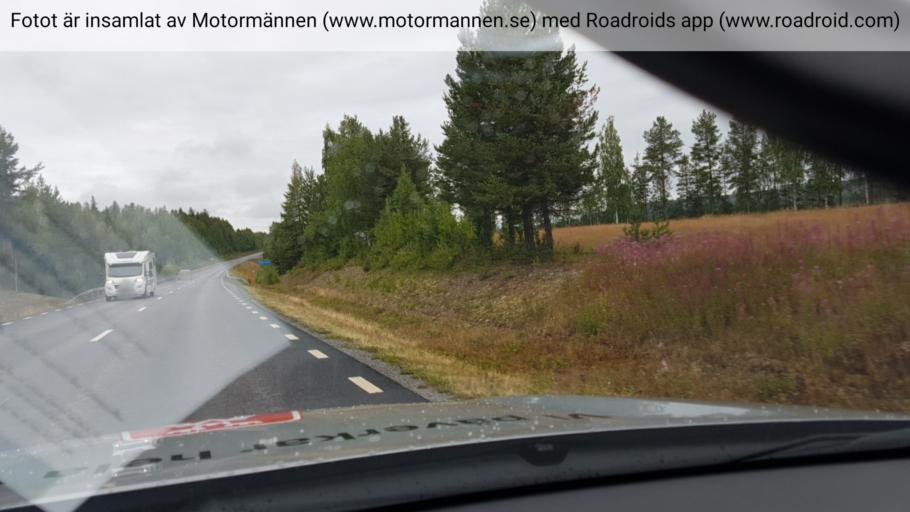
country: SE
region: Norrbotten
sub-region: Alvsbyns Kommun
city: AElvsbyn
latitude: 66.2618
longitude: 20.8371
